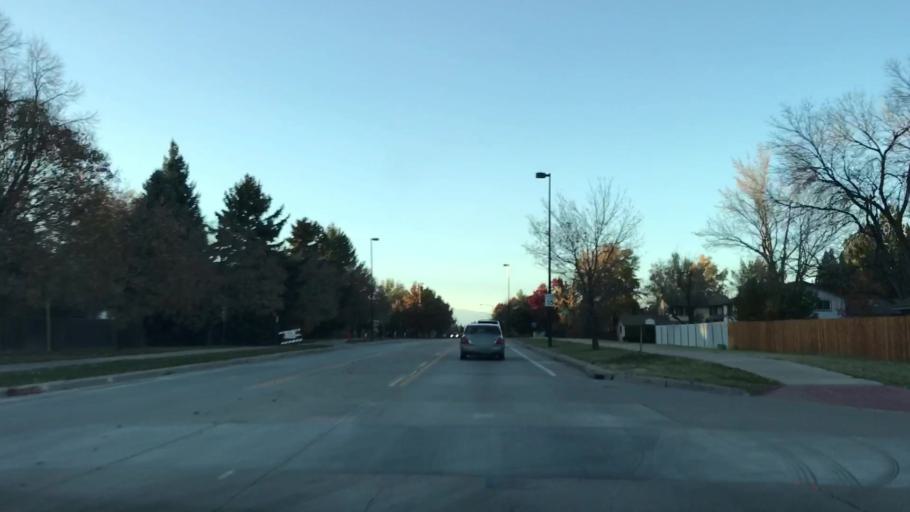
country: US
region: Colorado
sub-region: Arapahoe County
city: Glendale
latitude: 39.6634
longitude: -104.8890
